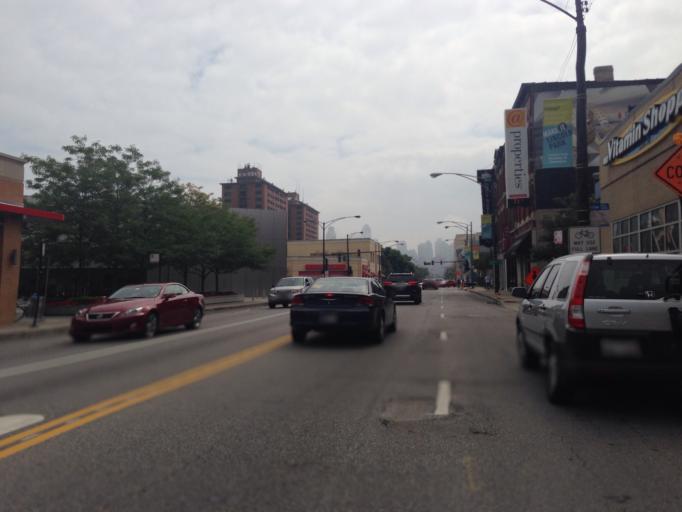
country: US
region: Illinois
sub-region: Cook County
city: Chicago
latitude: 41.9107
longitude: -87.6491
